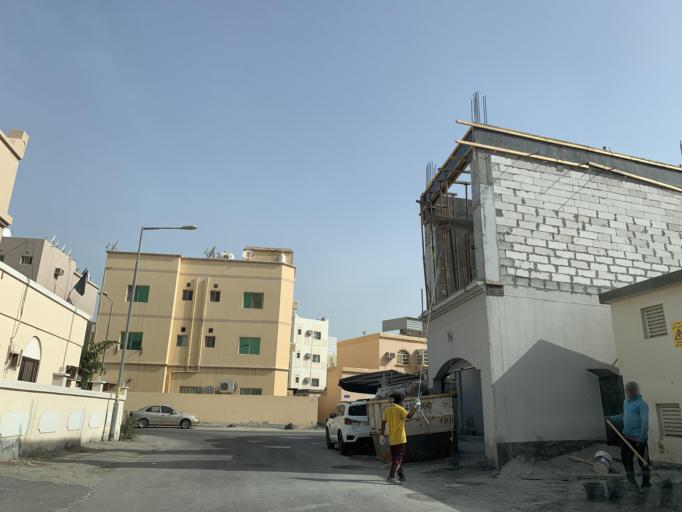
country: BH
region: Northern
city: Madinat `Isa
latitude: 26.1795
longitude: 50.5637
